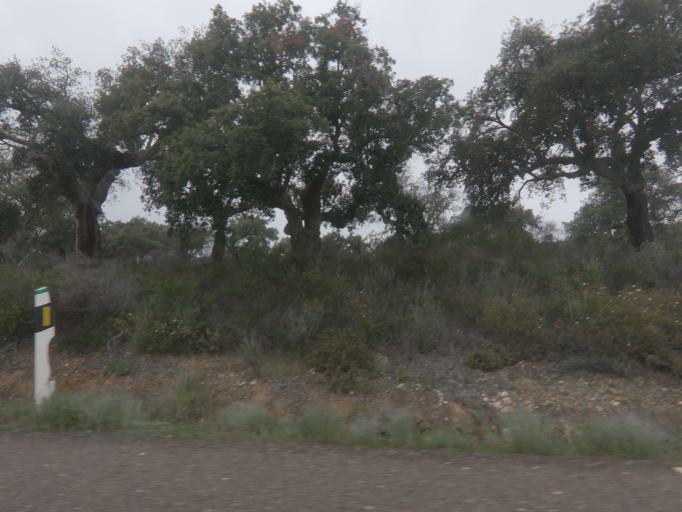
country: ES
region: Extremadura
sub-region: Provincia de Badajoz
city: Puebla de Obando
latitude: 39.1897
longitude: -6.5972
